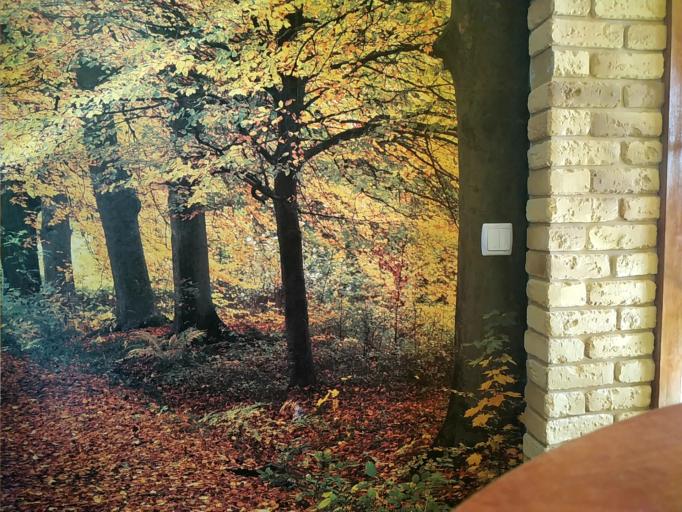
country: RU
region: Jaroslavl
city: Kukoboy
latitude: 58.8259
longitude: 39.7596
